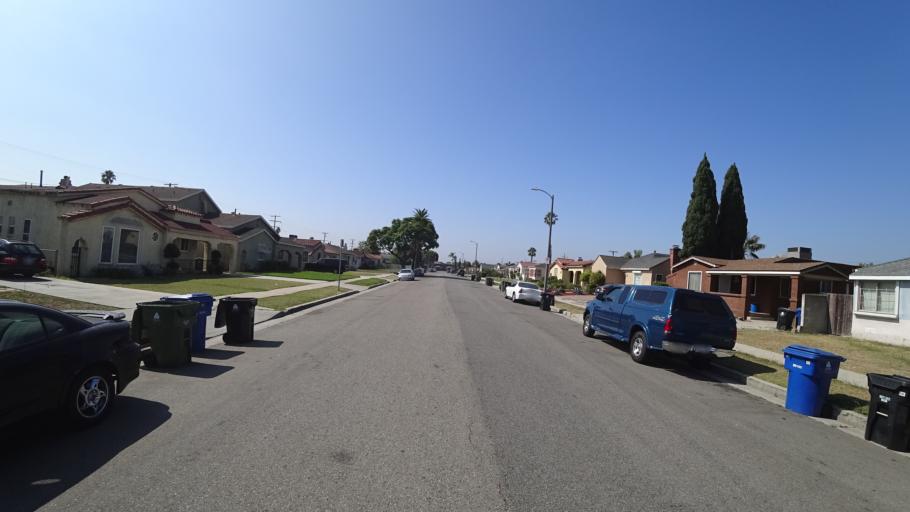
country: US
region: California
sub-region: Los Angeles County
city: Westmont
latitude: 33.9445
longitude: -118.3057
